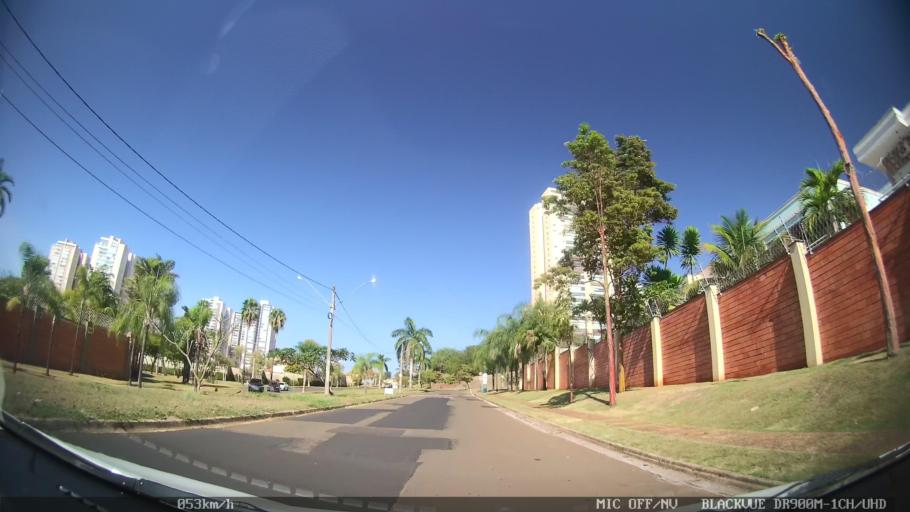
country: BR
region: Sao Paulo
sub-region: Ribeirao Preto
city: Ribeirao Preto
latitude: -21.2144
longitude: -47.8016
